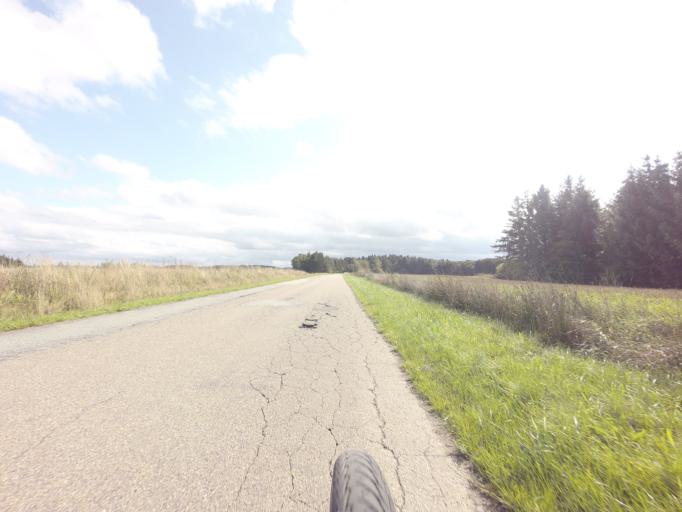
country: DK
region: North Denmark
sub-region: Hjorring Kommune
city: Hirtshals
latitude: 57.5425
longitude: 10.0574
